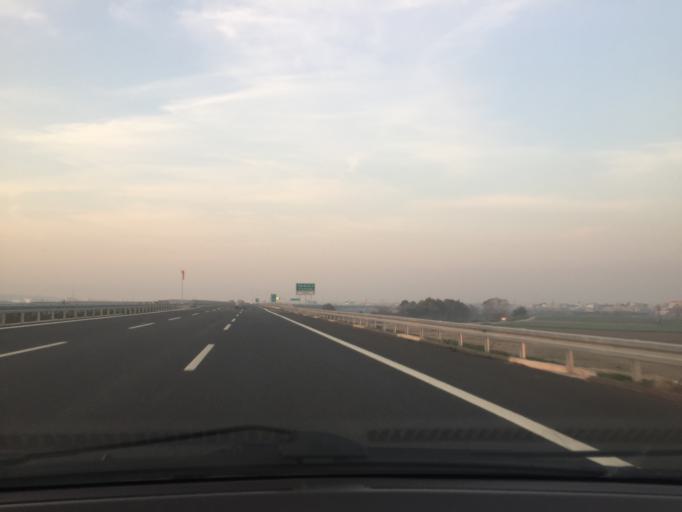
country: TR
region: Bursa
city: Karacabey
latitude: 40.2031
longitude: 28.3767
